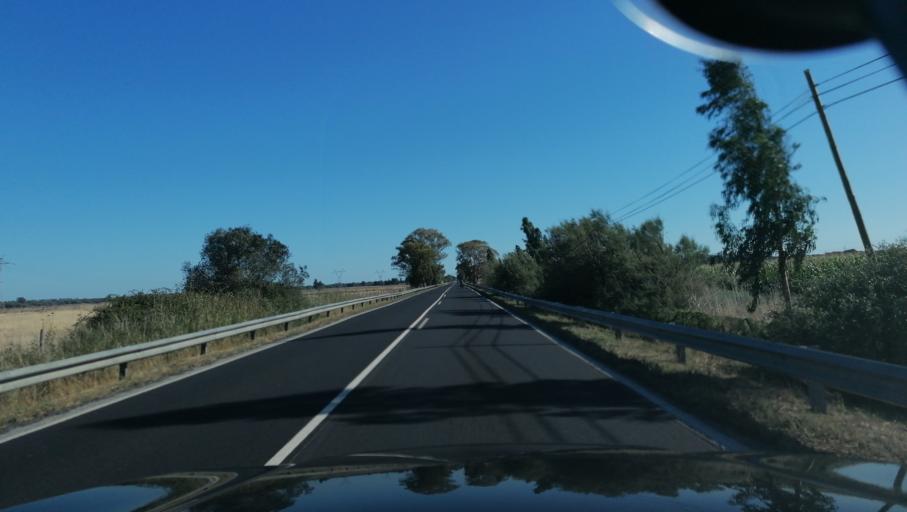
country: PT
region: Santarem
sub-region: Benavente
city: Samora Correia
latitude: 38.8781
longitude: -8.8813
